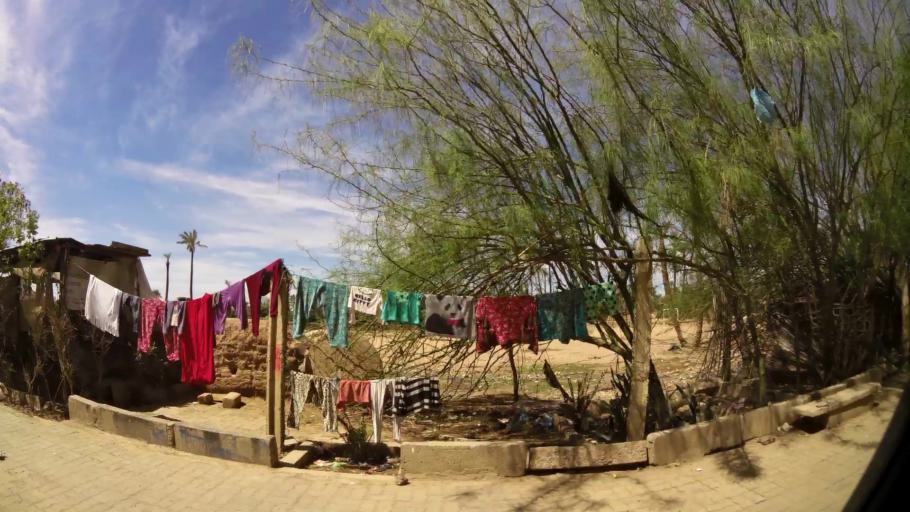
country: MA
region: Marrakech-Tensift-Al Haouz
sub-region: Marrakech
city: Marrakesh
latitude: 31.6668
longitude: -7.9871
